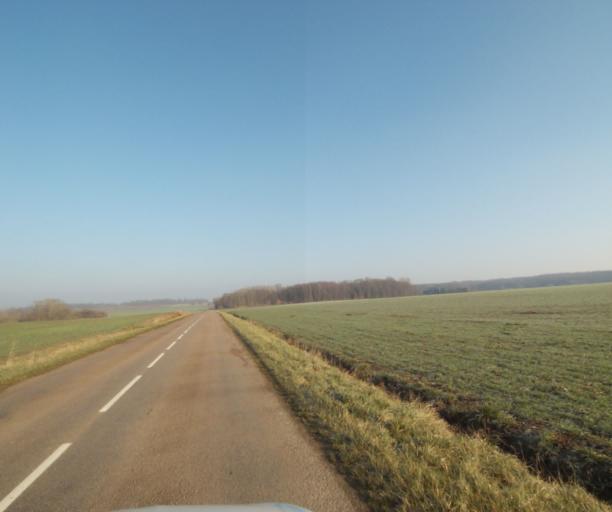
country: FR
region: Champagne-Ardenne
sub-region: Departement de la Haute-Marne
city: Montier-en-Der
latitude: 48.4167
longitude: 4.7427
